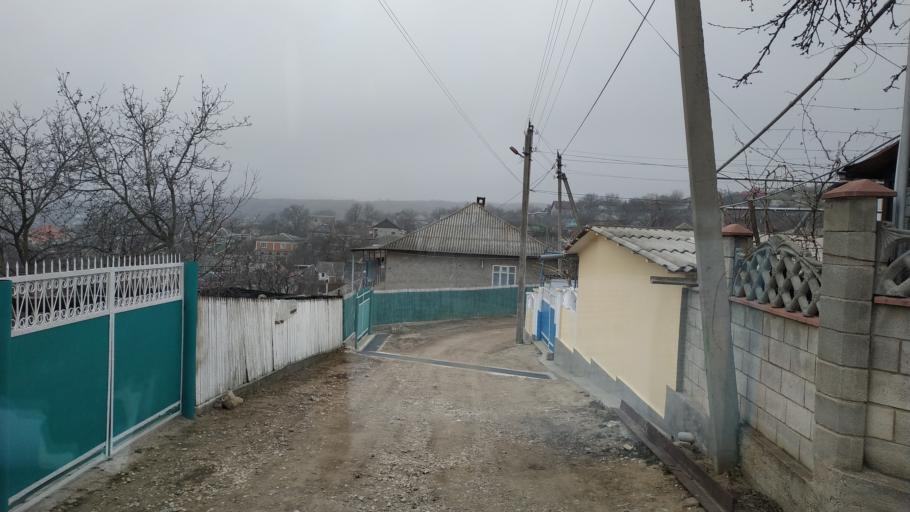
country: MD
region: Hincesti
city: Hincesti
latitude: 46.9075
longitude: 28.6666
